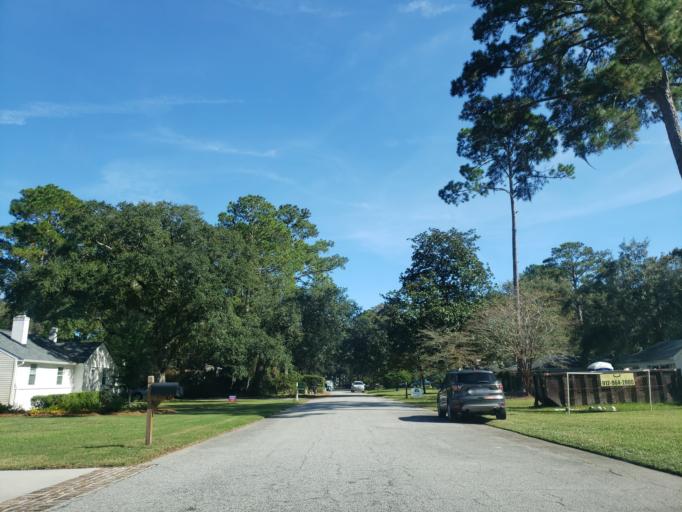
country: US
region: Georgia
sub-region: Chatham County
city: Isle of Hope
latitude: 31.9745
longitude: -81.0622
